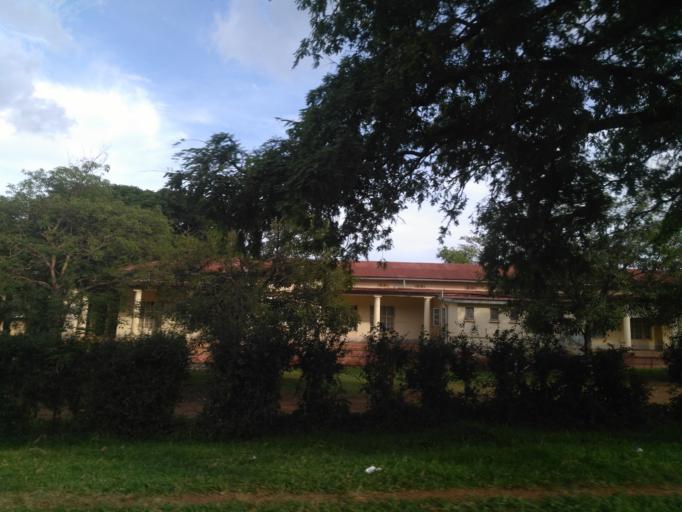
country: UG
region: Eastern Region
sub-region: Jinja District
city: Jinja
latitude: 0.4221
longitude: 33.2060
